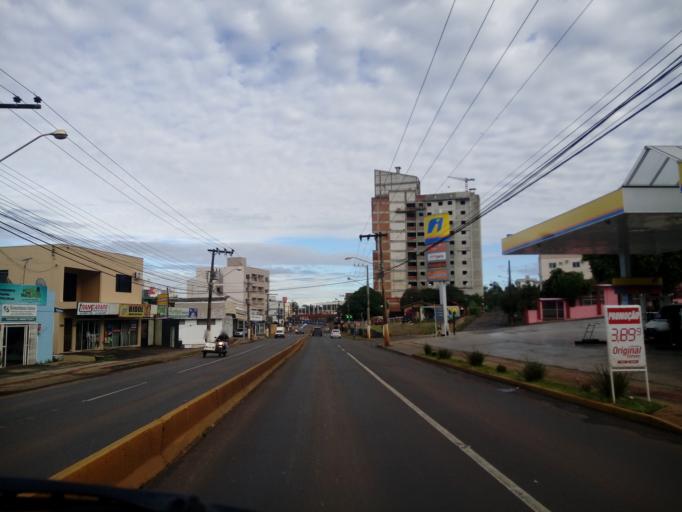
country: BR
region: Santa Catarina
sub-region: Chapeco
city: Chapeco
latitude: -27.0953
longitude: -52.6324
